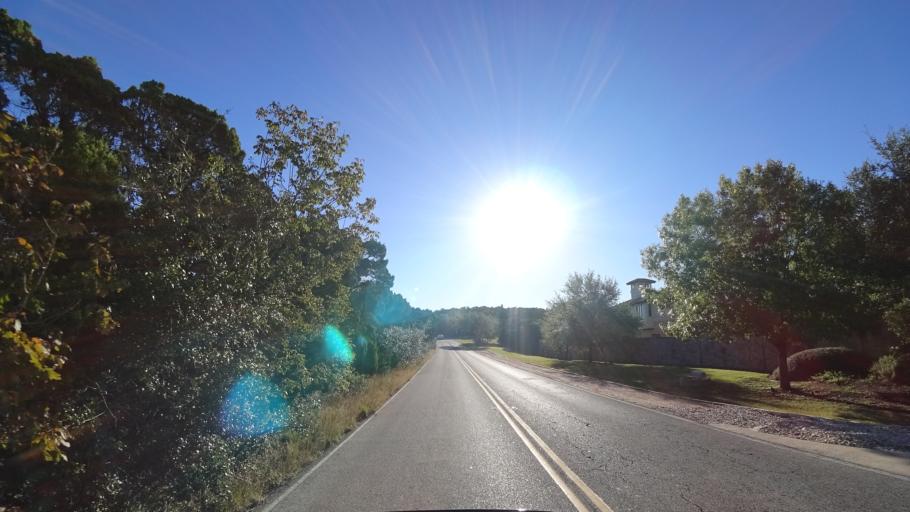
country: US
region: Texas
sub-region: Travis County
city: West Lake Hills
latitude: 30.3623
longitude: -97.8127
